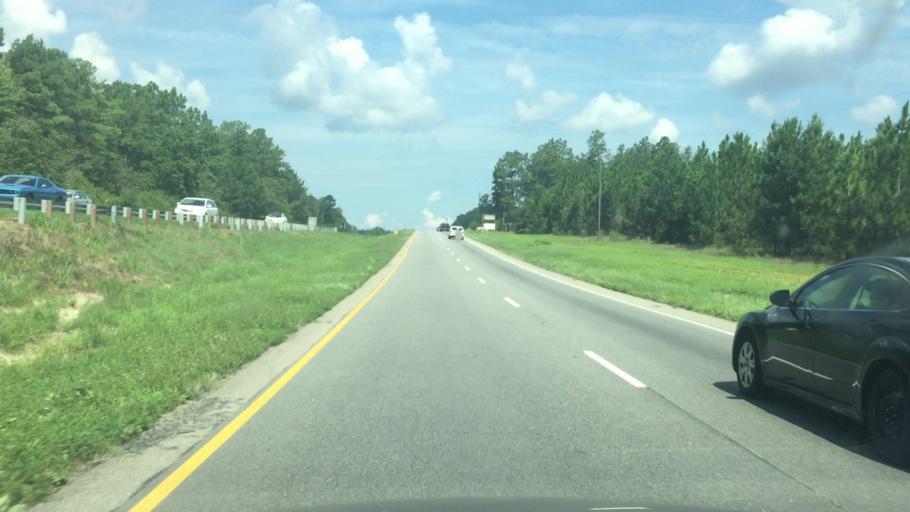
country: US
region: North Carolina
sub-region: Richmond County
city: Hamlet
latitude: 34.8615
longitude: -79.6332
